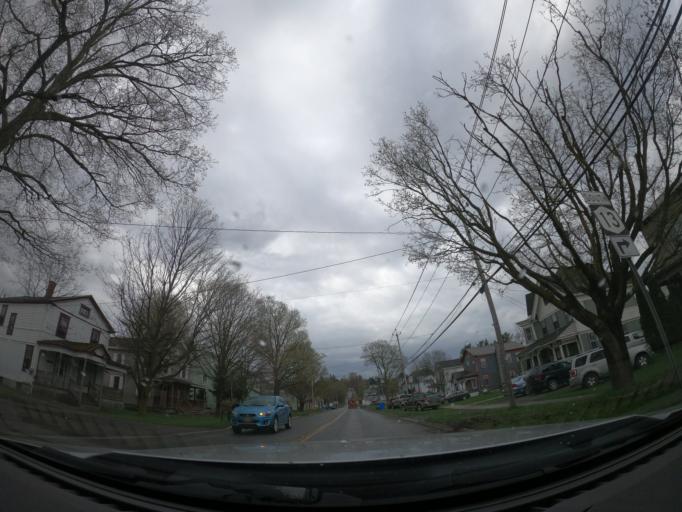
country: US
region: New York
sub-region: Madison County
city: Cazenovia
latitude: 42.7586
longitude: -75.8843
